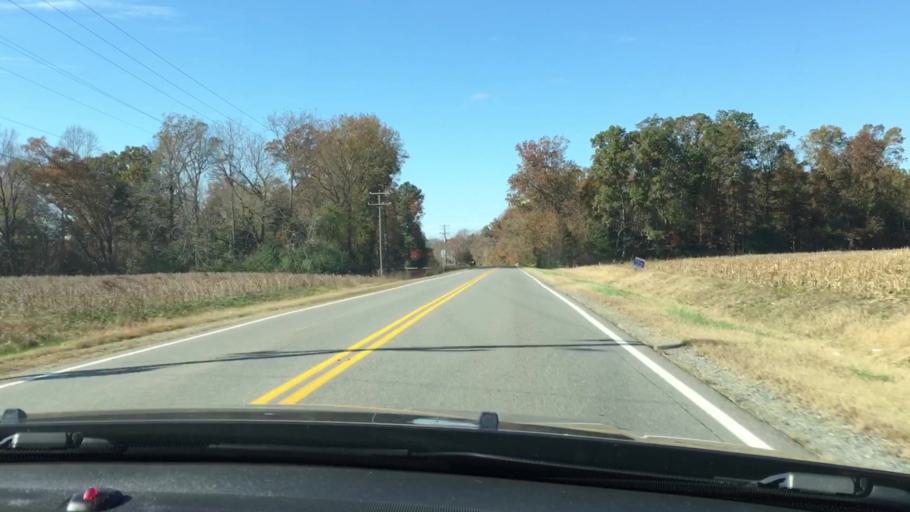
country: US
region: Virginia
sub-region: King William County
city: King William
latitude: 37.7104
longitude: -77.0573
